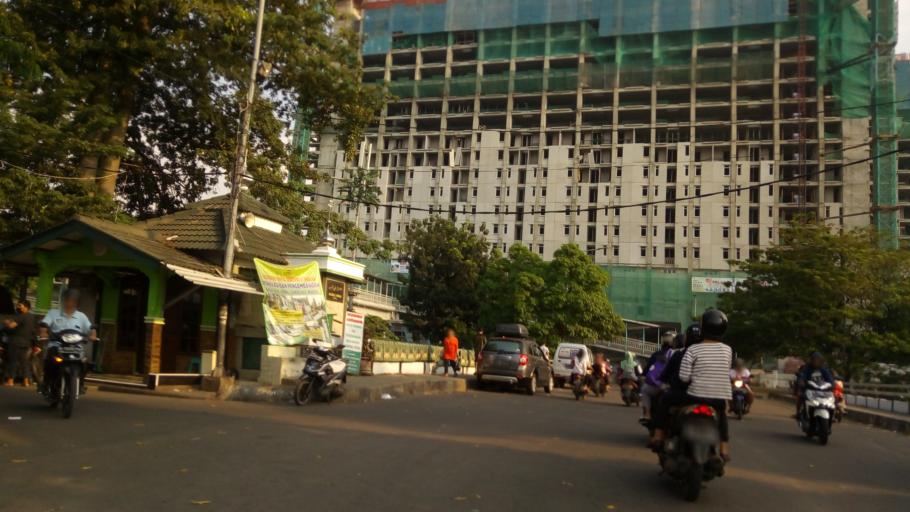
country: ID
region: Jakarta Raya
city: Jakarta
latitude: -6.2062
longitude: 106.8413
